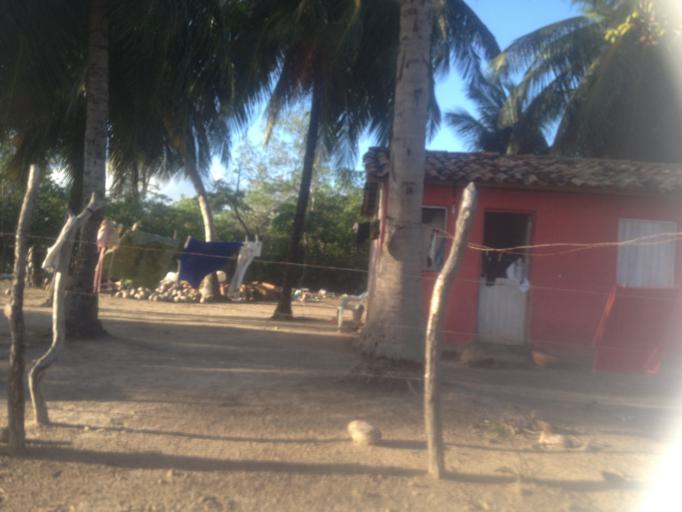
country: BR
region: Sergipe
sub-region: Indiaroba
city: Indiaroba
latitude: -11.4644
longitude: -37.3599
